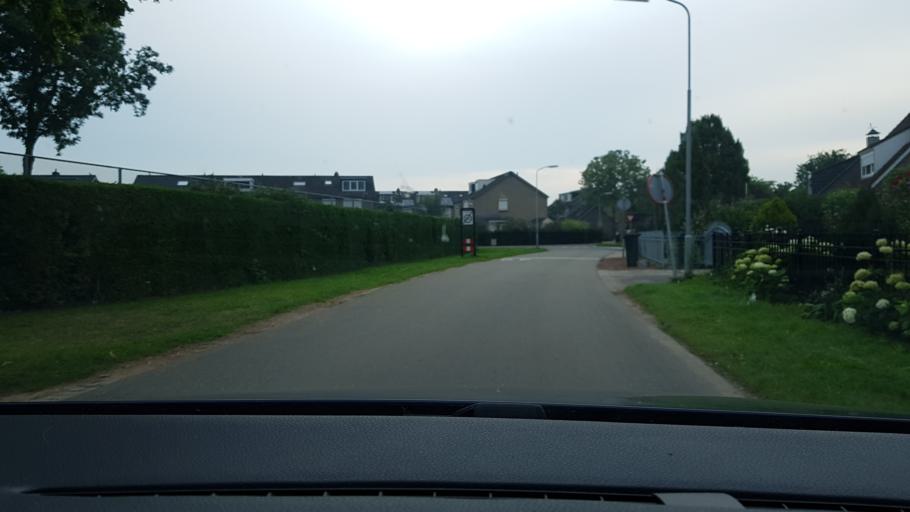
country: NL
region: Gelderland
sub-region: Gemeente Beuningen
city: Beuningen
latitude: 51.8573
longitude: 5.7789
